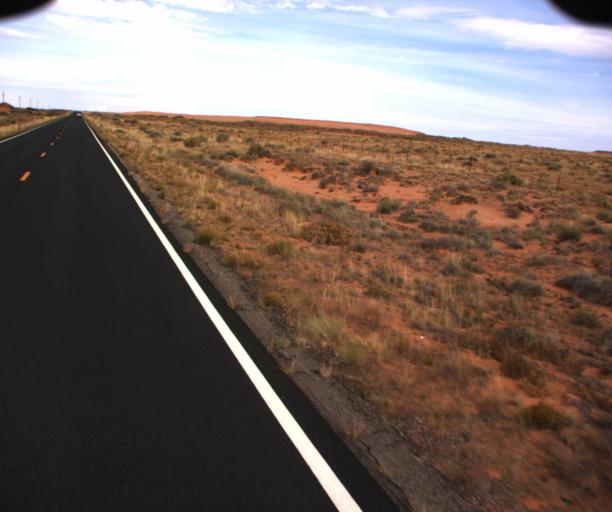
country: US
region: Arizona
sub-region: Apache County
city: Many Farms
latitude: 36.8174
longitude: -109.6459
